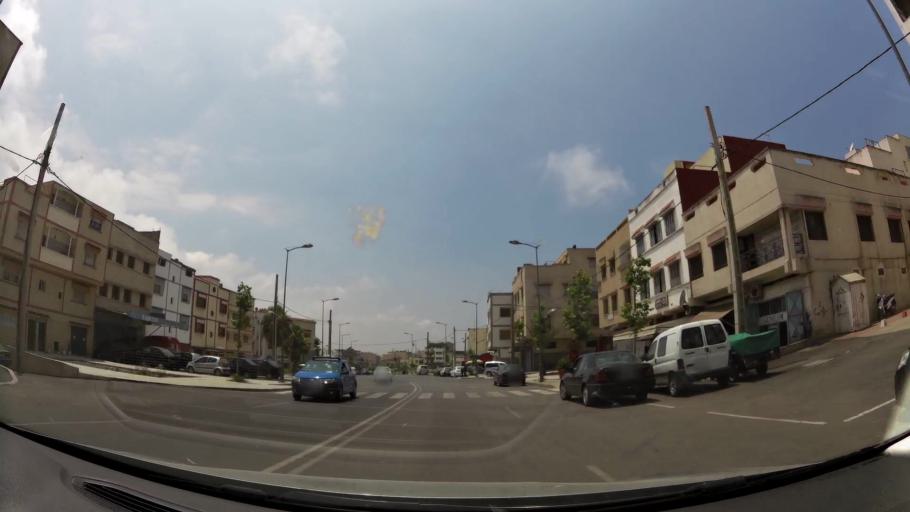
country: MA
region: Rabat-Sale-Zemmour-Zaer
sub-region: Skhirate-Temara
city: Temara
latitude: 33.9797
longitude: -6.8888
